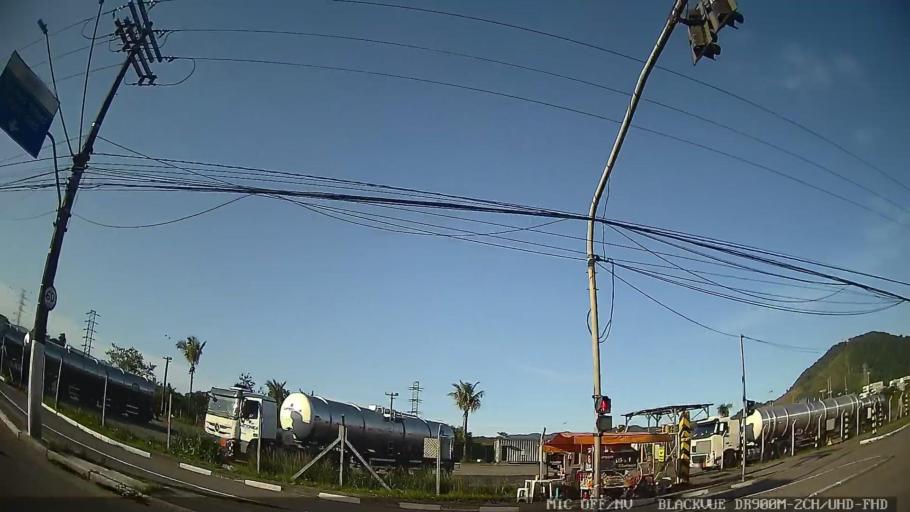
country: BR
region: Sao Paulo
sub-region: Guaruja
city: Guaruja
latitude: -23.9767
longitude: -46.2733
